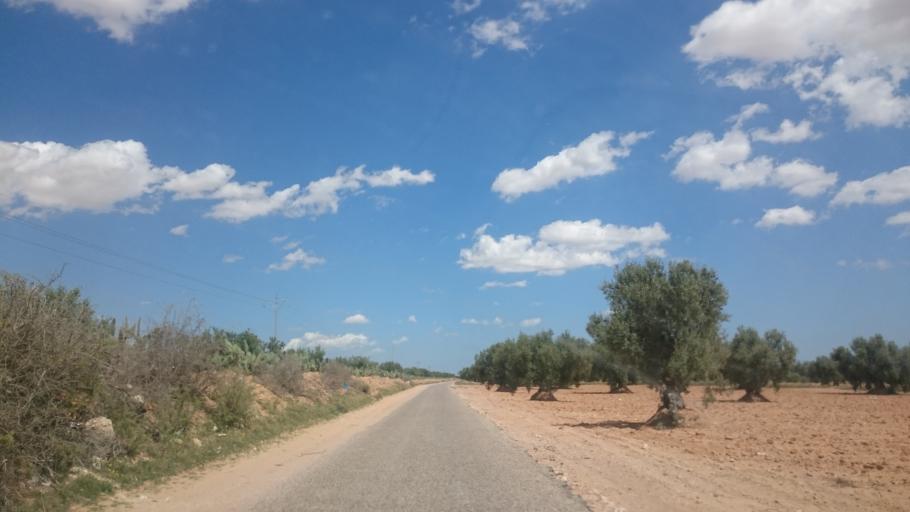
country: TN
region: Safaqis
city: Sfax
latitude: 34.6957
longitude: 10.5813
